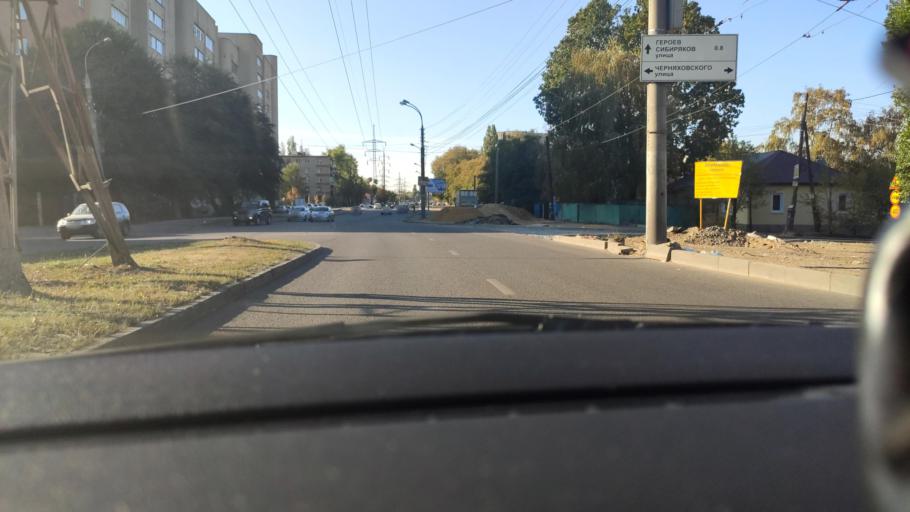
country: RU
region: Voronezj
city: Voronezh
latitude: 51.6393
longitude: 39.1627
